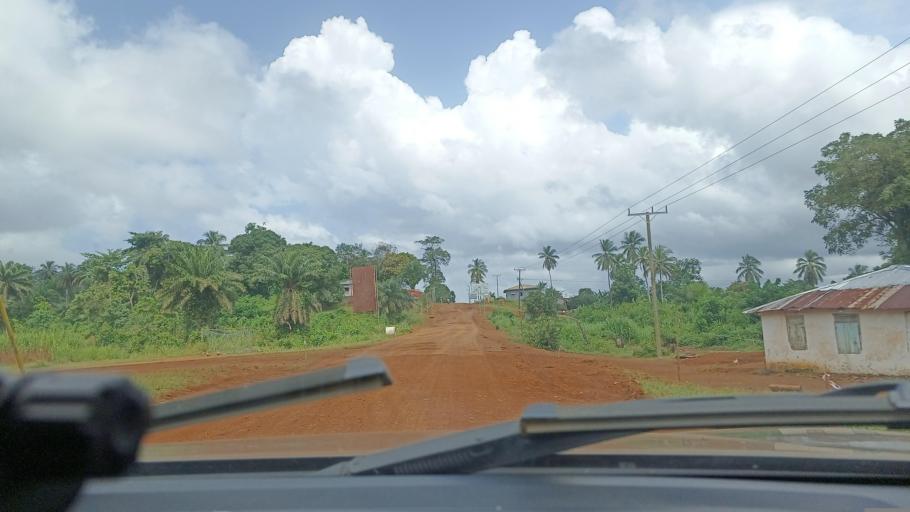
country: LR
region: Grand Cape Mount
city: Robertsport
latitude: 6.7512
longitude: -11.3622
